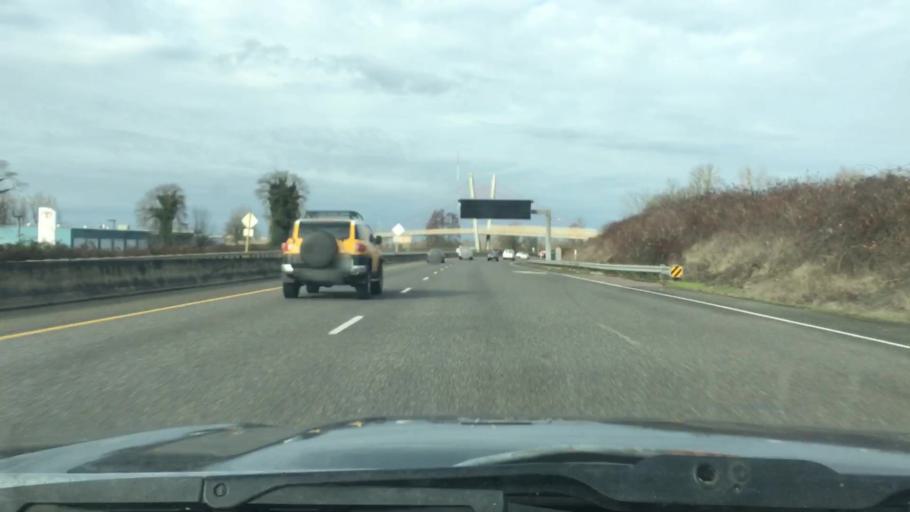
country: US
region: Oregon
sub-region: Lane County
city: Eugene
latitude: 44.0739
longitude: -123.1044
